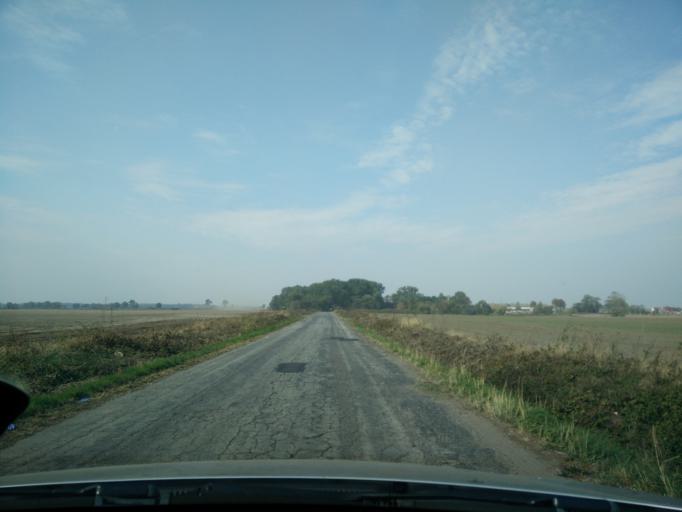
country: PL
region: Greater Poland Voivodeship
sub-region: Powiat sredzki
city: Dominowo
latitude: 52.2836
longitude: 17.3226
